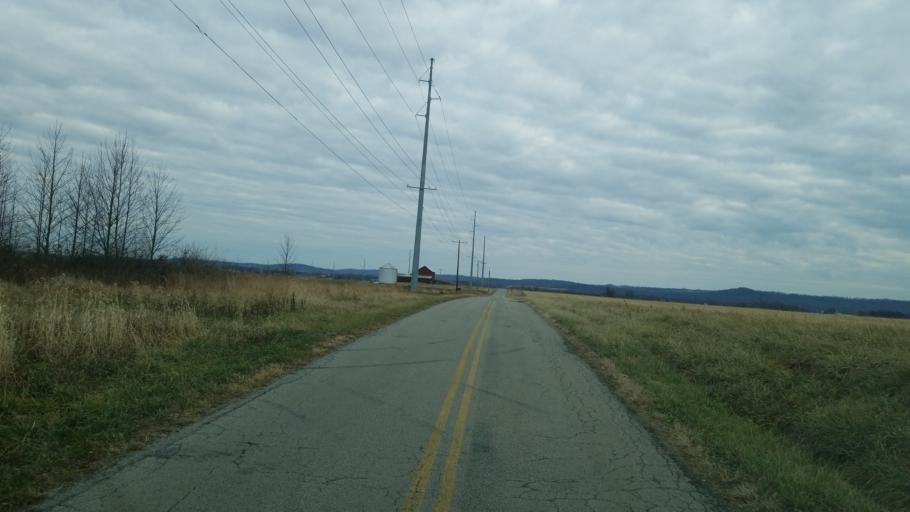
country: US
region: Ohio
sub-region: Highland County
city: Greenfield
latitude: 39.3220
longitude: -83.3712
